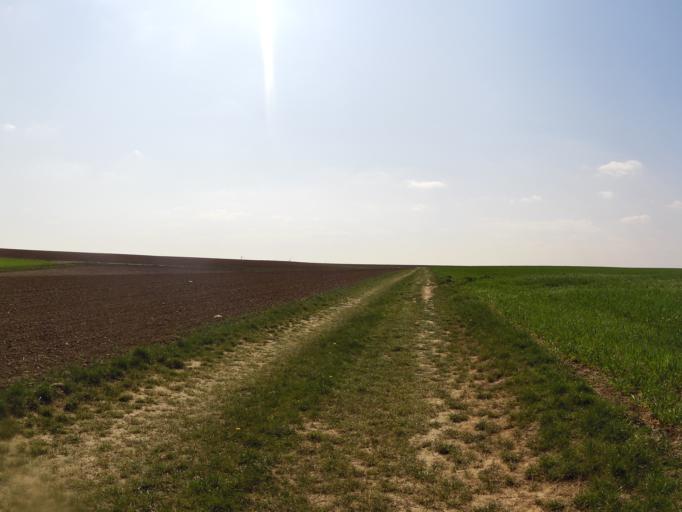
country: DE
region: Bavaria
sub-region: Regierungsbezirk Unterfranken
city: Dettelbach
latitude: 49.8171
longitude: 10.1389
